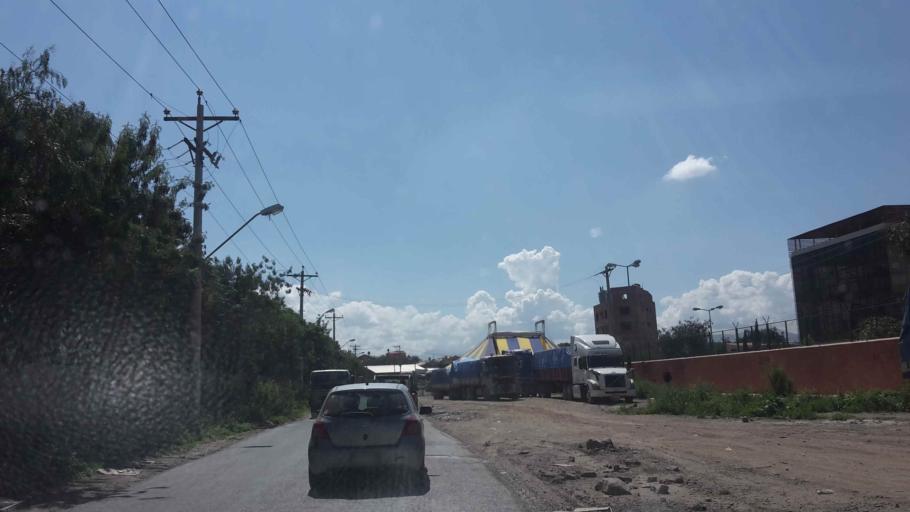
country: BO
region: Cochabamba
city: Cochabamba
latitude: -17.3493
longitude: -66.1863
